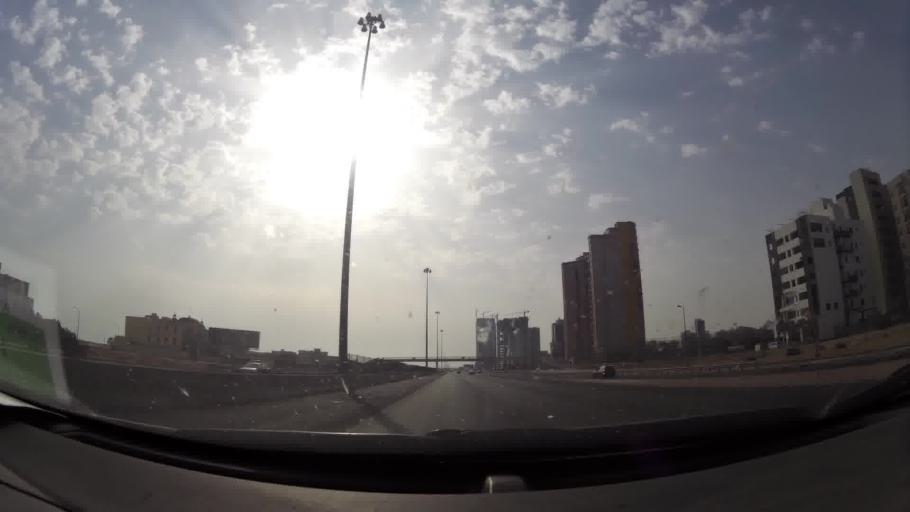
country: KW
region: Mubarak al Kabir
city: Sabah as Salim
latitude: 29.2635
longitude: 48.0860
